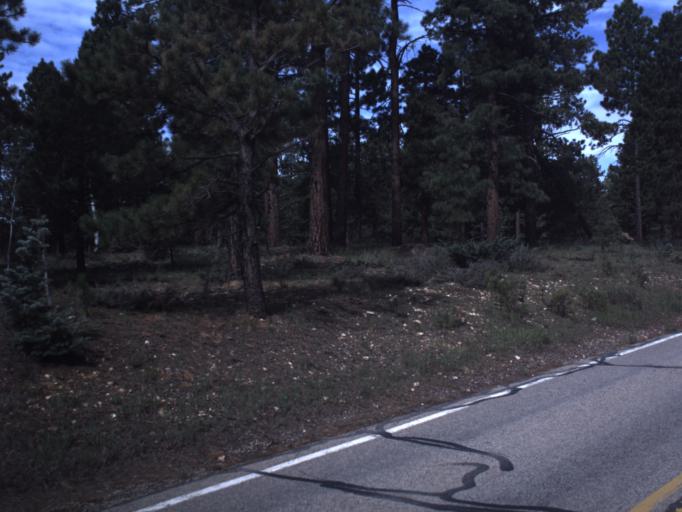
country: US
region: Utah
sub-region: Garfield County
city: Panguitch
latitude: 37.5163
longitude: -112.6437
